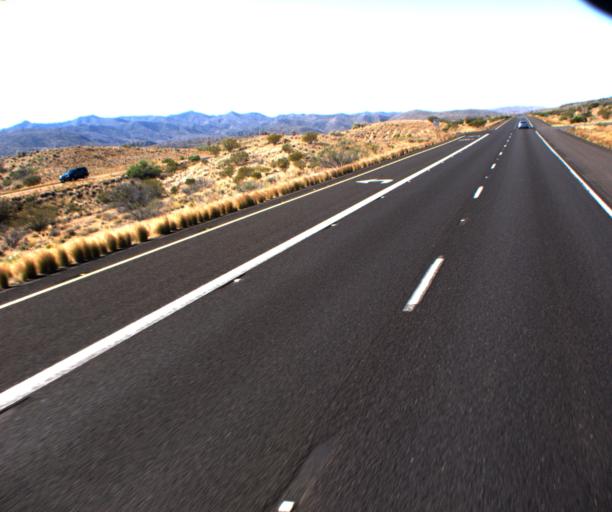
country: US
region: Arizona
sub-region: Mohave County
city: Kingman
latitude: 35.0580
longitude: -113.6656
